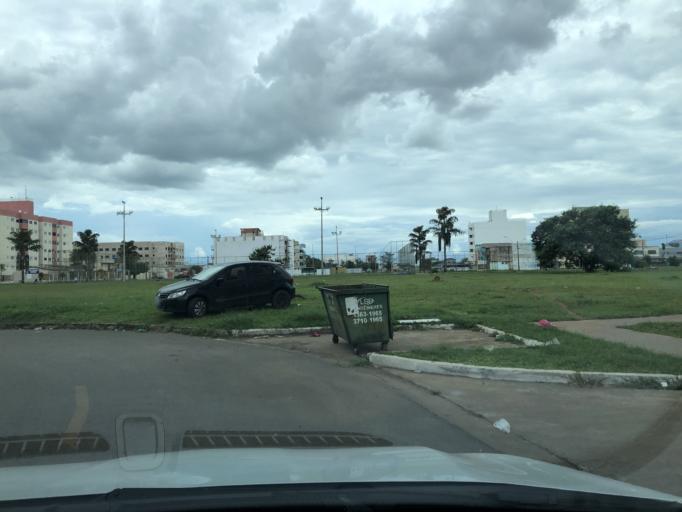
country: BR
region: Federal District
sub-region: Brasilia
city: Brasilia
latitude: -15.8688
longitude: -48.0652
